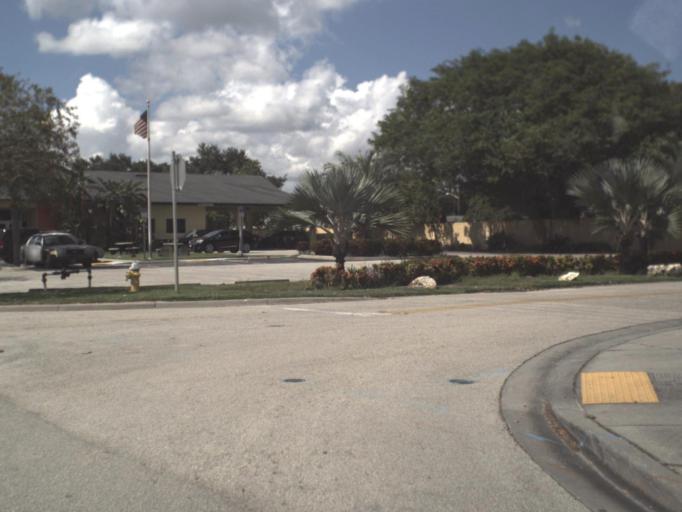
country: US
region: Florida
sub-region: Lee County
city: Fort Myers
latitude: 26.6410
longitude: -81.8531
